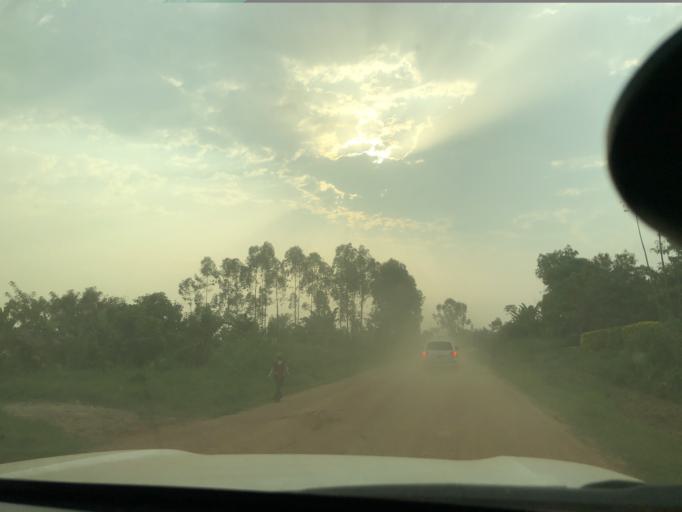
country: UG
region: Western Region
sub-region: Kasese District
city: Margherita
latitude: 0.3414
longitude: 29.6650
